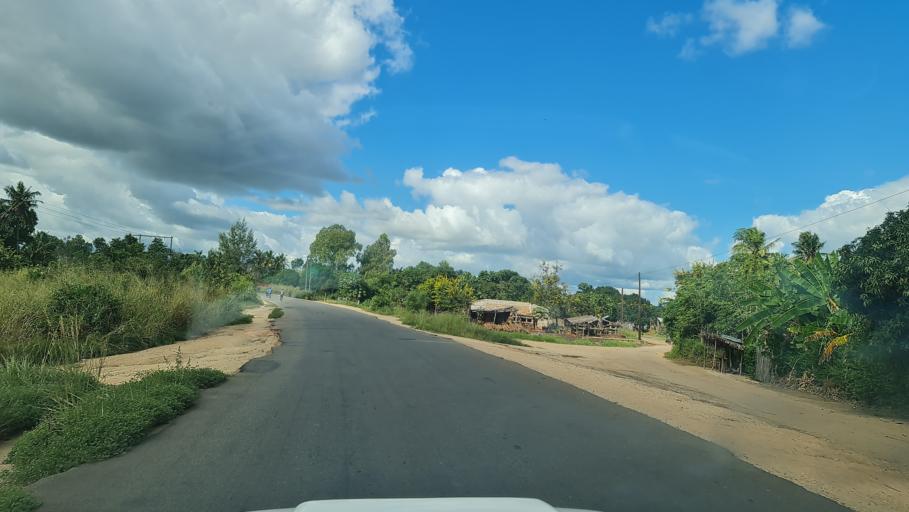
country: MZ
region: Zambezia
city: Quelimane
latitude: -17.6010
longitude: 36.8023
